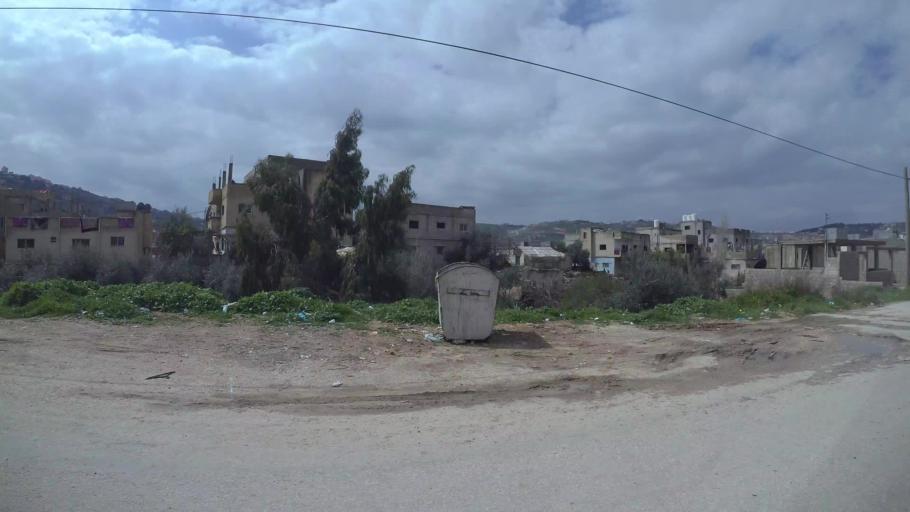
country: JO
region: Amman
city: Al Jubayhah
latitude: 32.0506
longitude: 35.8235
